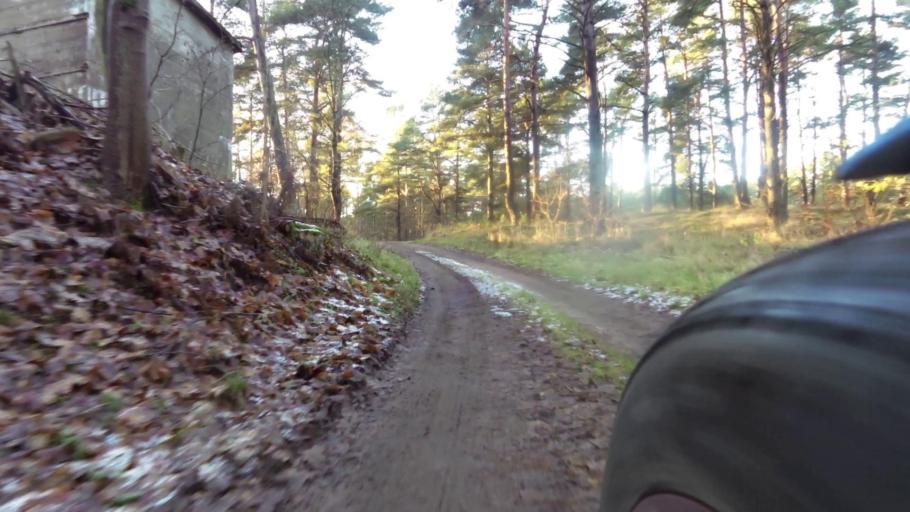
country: PL
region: West Pomeranian Voivodeship
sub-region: Powiat szczecinecki
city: Borne Sulinowo
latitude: 53.5934
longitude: 16.5164
